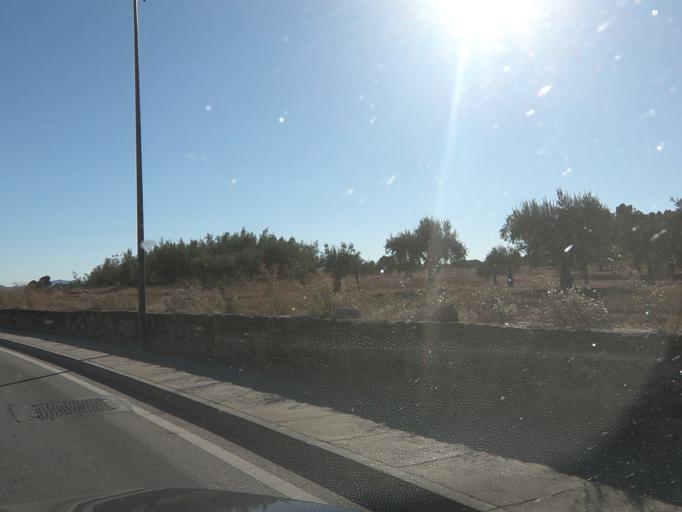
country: PT
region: Vila Real
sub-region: Valpacos
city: Valpacos
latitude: 41.5909
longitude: -7.3076
